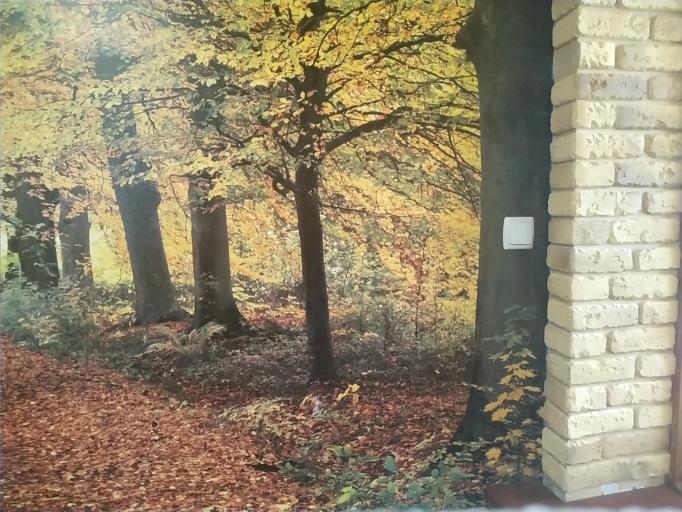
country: RU
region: Tverskaya
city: Vyshniy Volochek
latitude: 57.6210
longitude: 34.5850
